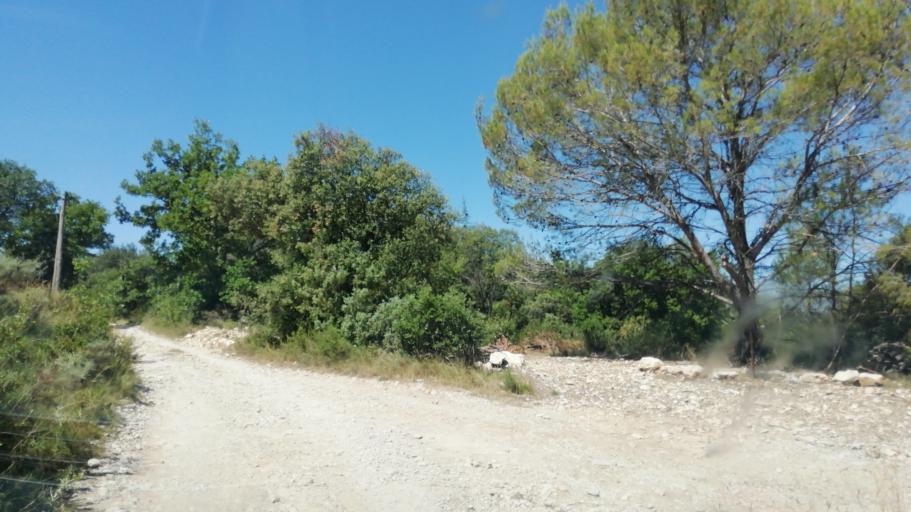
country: FR
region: Languedoc-Roussillon
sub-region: Departement de l'Herault
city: Saint-Martin-de-Londres
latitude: 43.8333
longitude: 3.7805
